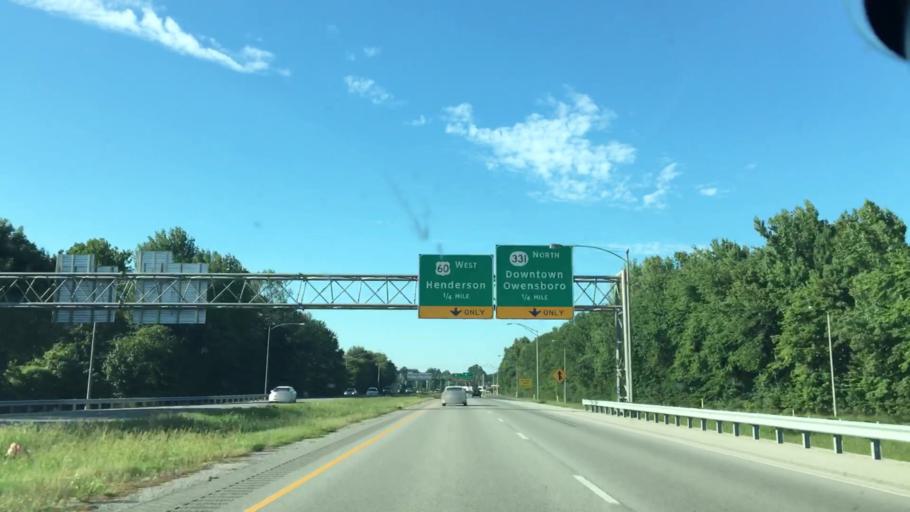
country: US
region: Kentucky
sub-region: Daviess County
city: Owensboro
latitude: 37.7691
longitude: -87.1645
